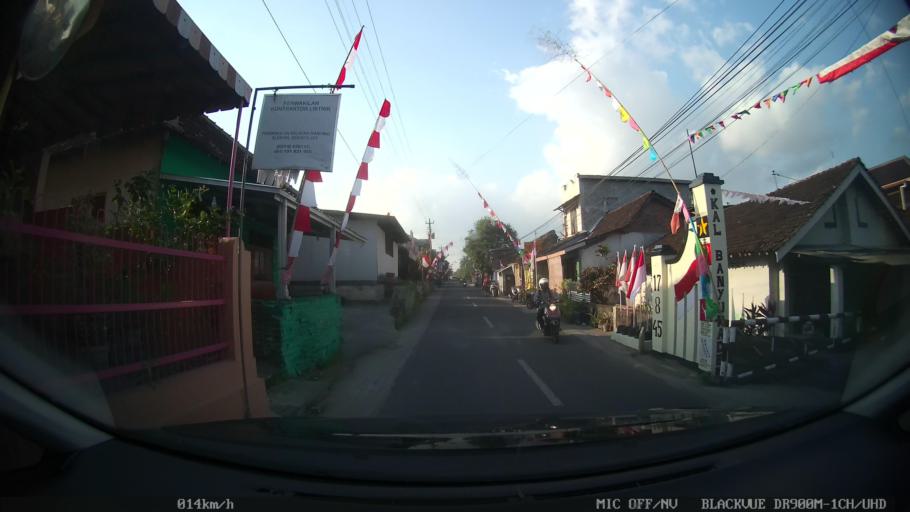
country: ID
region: Daerah Istimewa Yogyakarta
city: Gamping Lor
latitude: -7.7939
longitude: 110.3354
